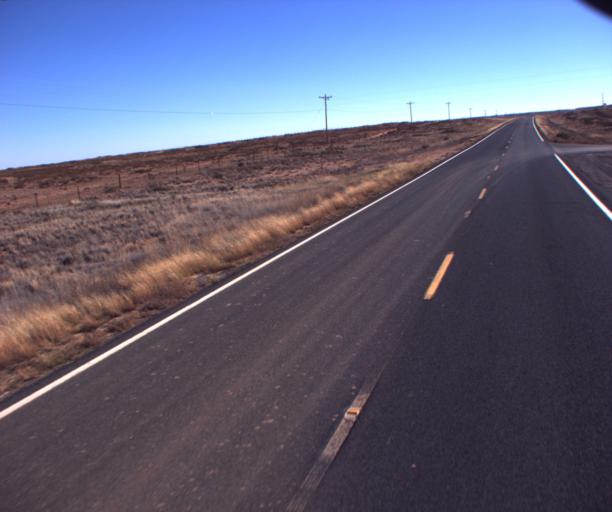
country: US
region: Arizona
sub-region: Coconino County
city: Tuba City
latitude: 36.0066
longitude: -111.0530
